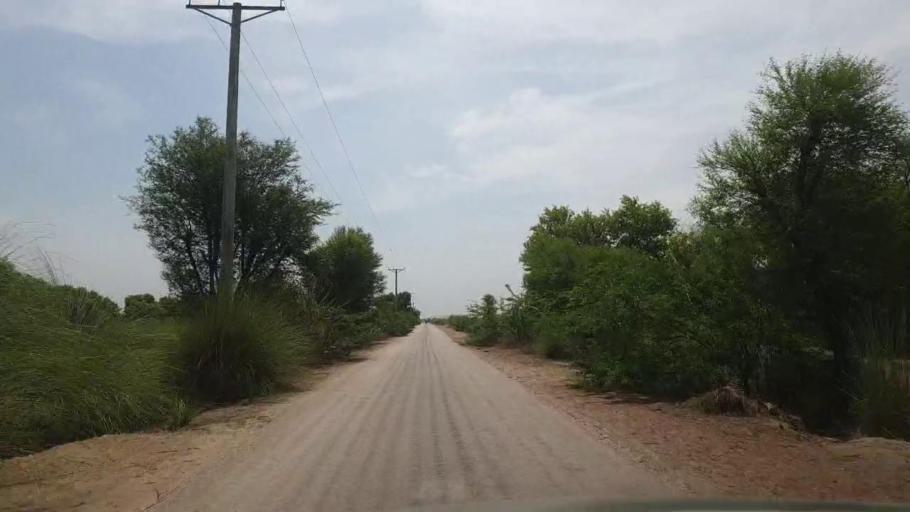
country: PK
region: Sindh
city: Kot Diji
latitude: 27.1187
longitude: 69.0059
